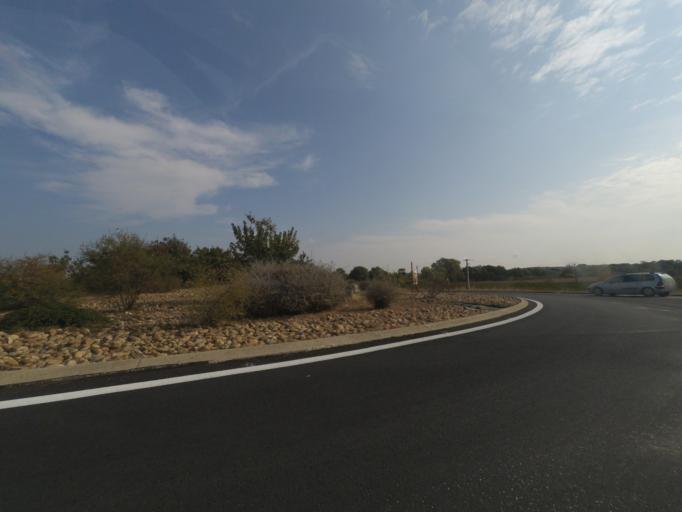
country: FR
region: Languedoc-Roussillon
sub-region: Departement de l'Herault
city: Boisseron
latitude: 43.7509
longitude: 4.0902
